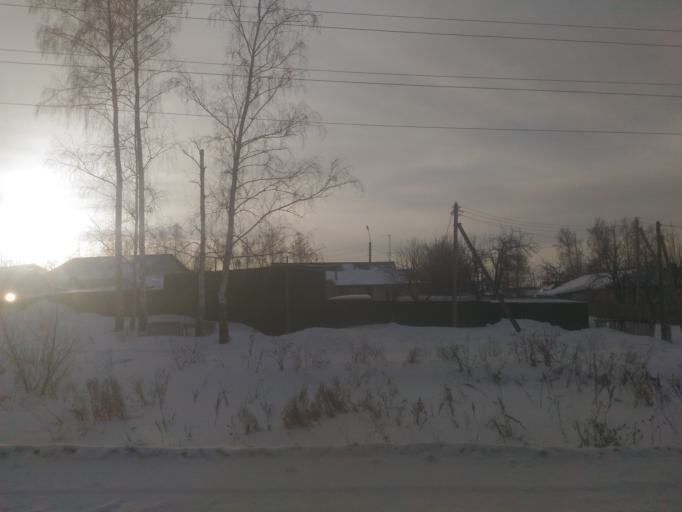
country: RU
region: Ulyanovsk
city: Isheyevka
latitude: 54.4299
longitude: 48.2801
